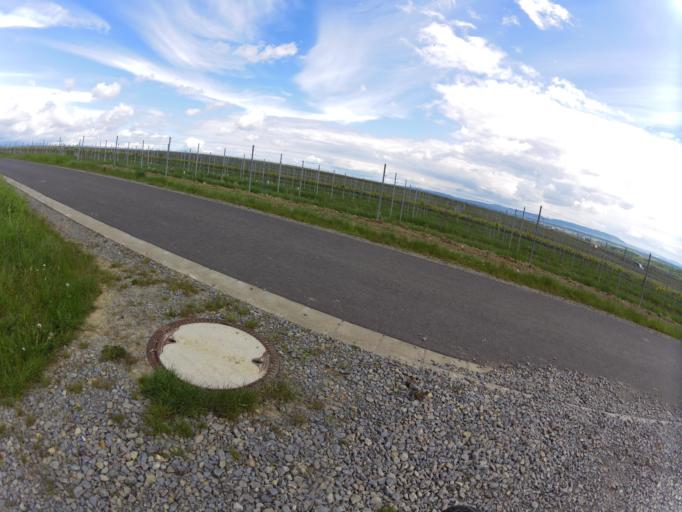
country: DE
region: Bavaria
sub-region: Regierungsbezirk Unterfranken
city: Sommerach
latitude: 49.8401
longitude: 10.1948
